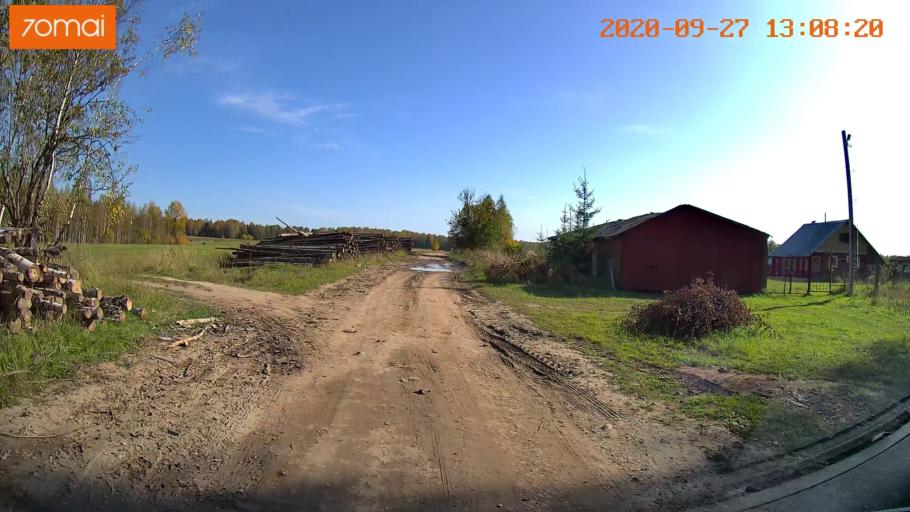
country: RU
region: Ivanovo
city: Furmanov
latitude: 57.1624
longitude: 41.0792
